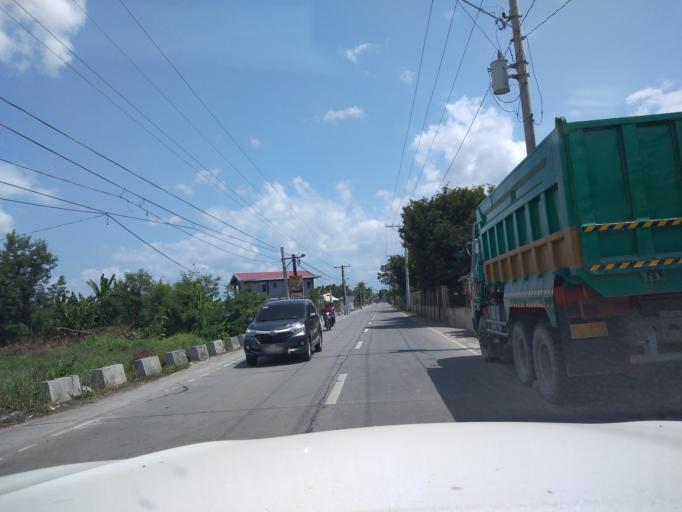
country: PH
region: Central Luzon
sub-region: Province of Pampanga
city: Lourdes
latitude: 15.0179
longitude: 120.8683
